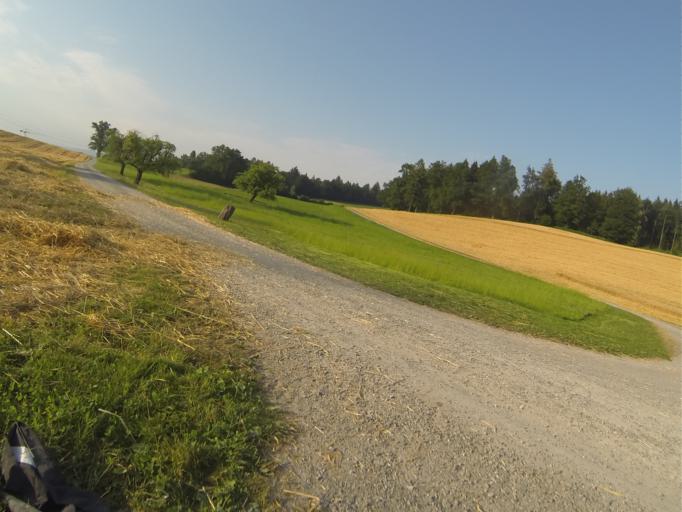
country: CH
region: Lucerne
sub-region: Lucerne-Stadt District
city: Luzern
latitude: 47.0739
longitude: 8.3135
